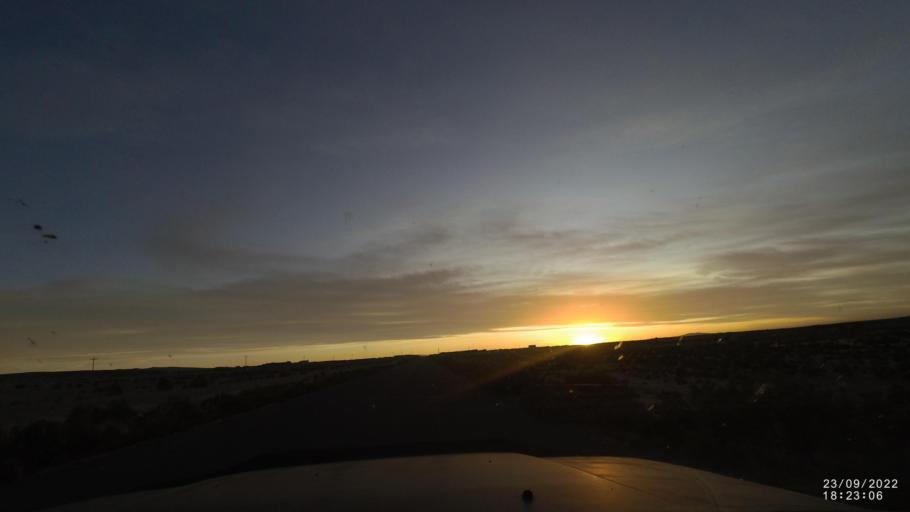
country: BO
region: Oruro
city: Challapata
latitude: -19.2928
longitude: -67.0975
